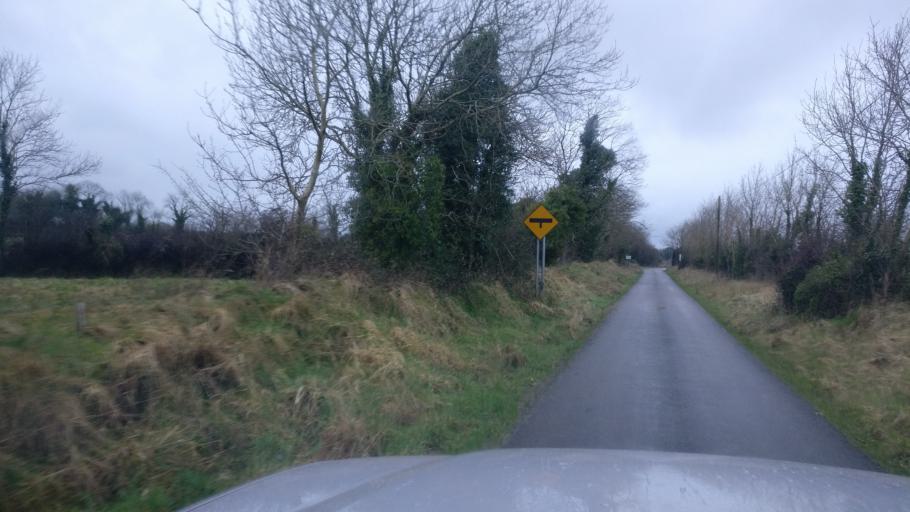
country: IE
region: Connaught
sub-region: County Galway
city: Ballinasloe
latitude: 53.2768
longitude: -8.3382
